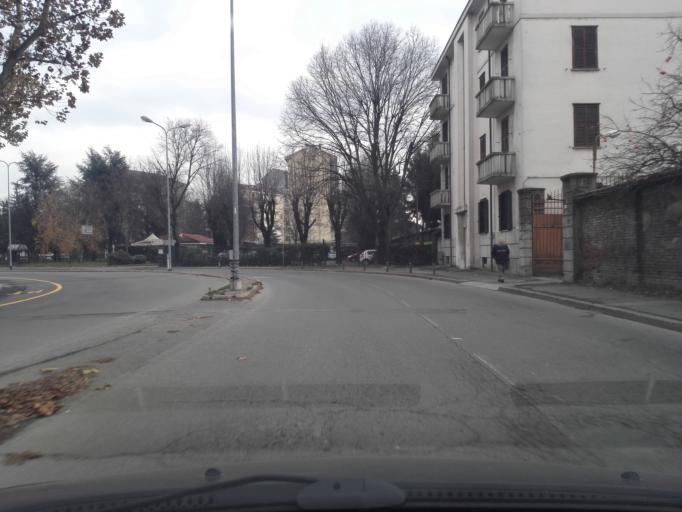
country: IT
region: Piedmont
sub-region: Provincia di Alessandria
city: Alessandria
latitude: 44.9074
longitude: 8.6097
